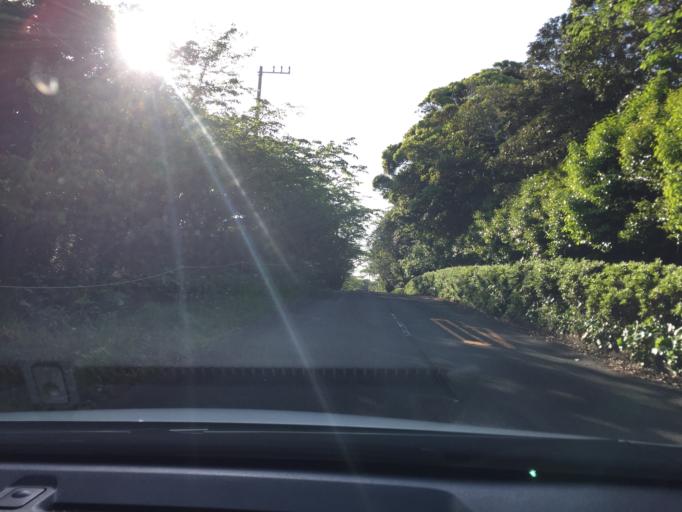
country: JP
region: Shizuoka
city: Shimoda
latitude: 34.6637
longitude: 138.9818
